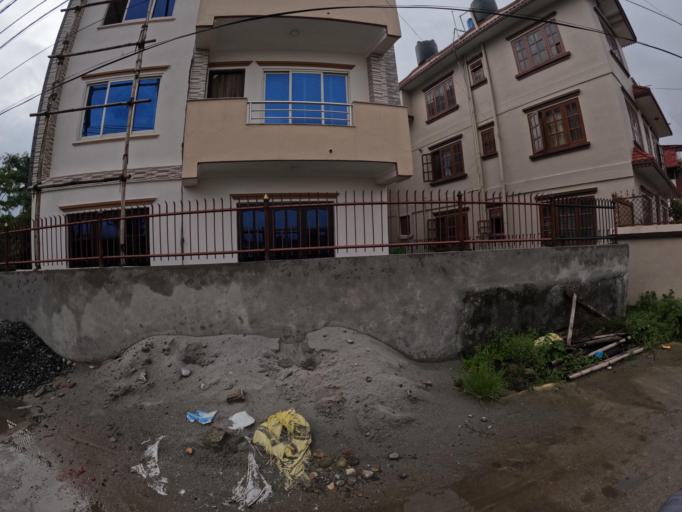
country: NP
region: Central Region
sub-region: Bagmati Zone
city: Kathmandu
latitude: 27.7594
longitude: 85.3231
